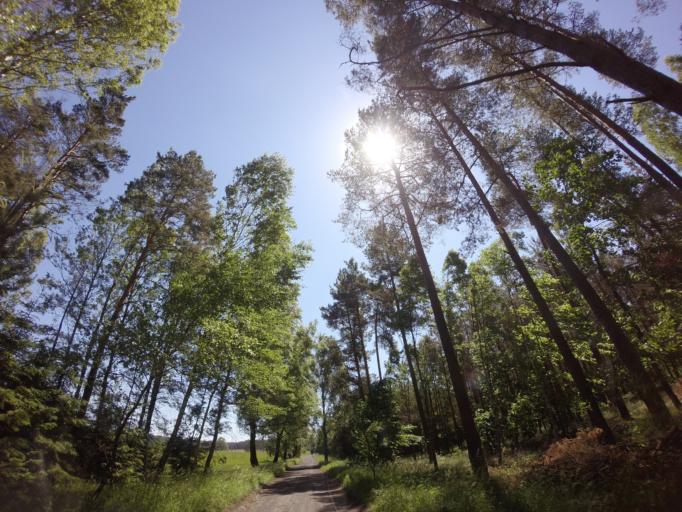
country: PL
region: West Pomeranian Voivodeship
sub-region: Powiat walecki
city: Miroslawiec
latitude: 53.2449
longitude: 16.0318
